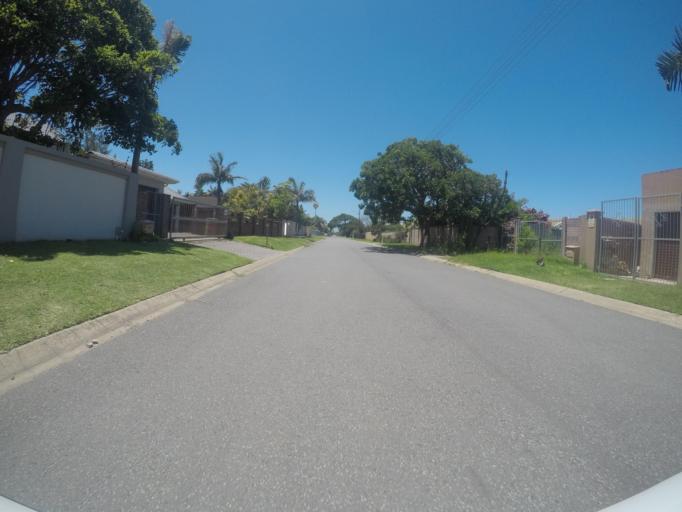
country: ZA
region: Eastern Cape
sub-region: Buffalo City Metropolitan Municipality
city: East London
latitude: -32.9503
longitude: 28.0112
